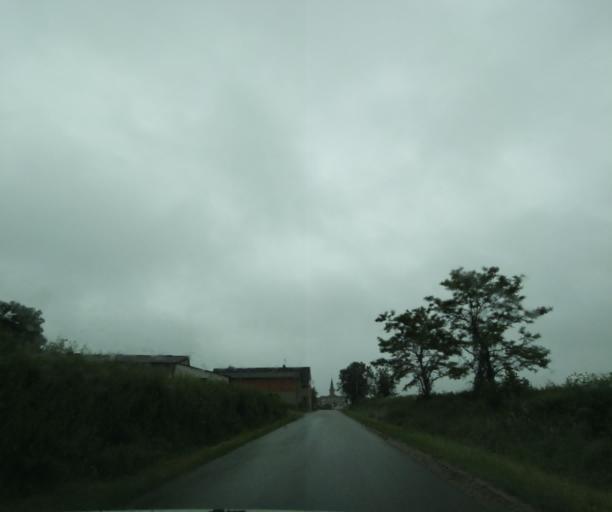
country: FR
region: Bourgogne
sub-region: Departement de Saone-et-Loire
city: Charolles
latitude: 46.4060
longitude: 4.2537
